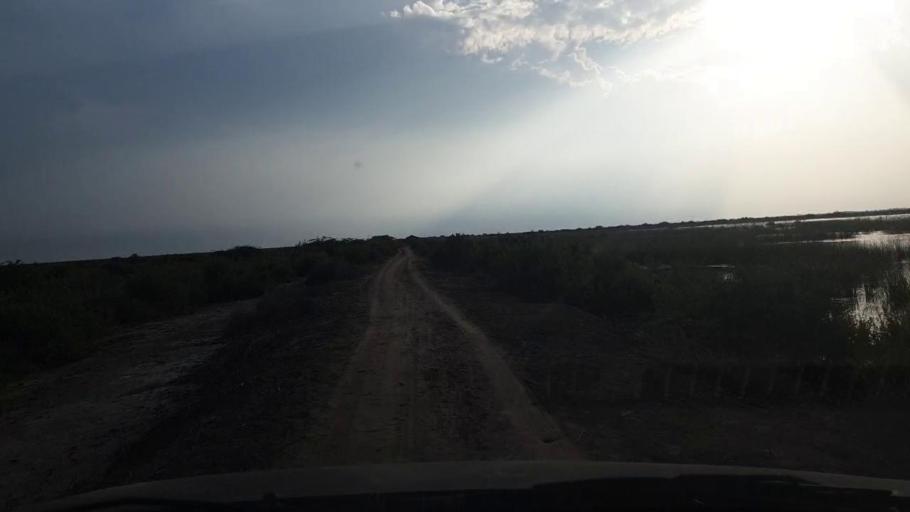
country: PK
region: Sindh
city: Badin
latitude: 24.4311
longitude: 68.6691
